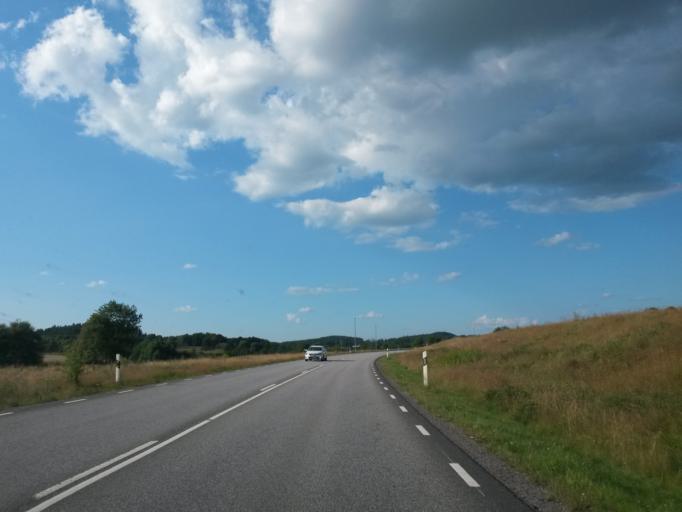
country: SE
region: Vaestra Goetaland
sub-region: Lerums Kommun
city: Stenkullen
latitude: 57.7854
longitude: 12.2961
